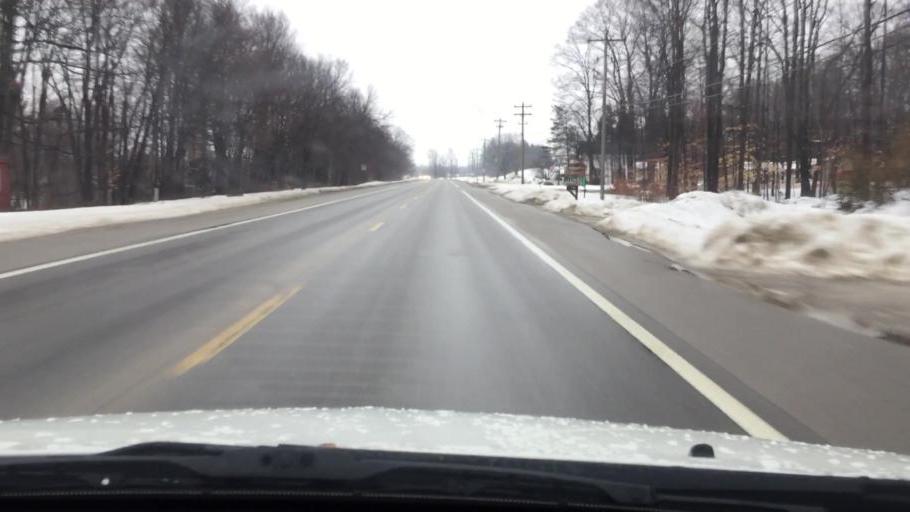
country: US
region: Michigan
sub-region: Charlevoix County
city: Charlevoix
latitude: 45.2871
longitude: -85.2440
